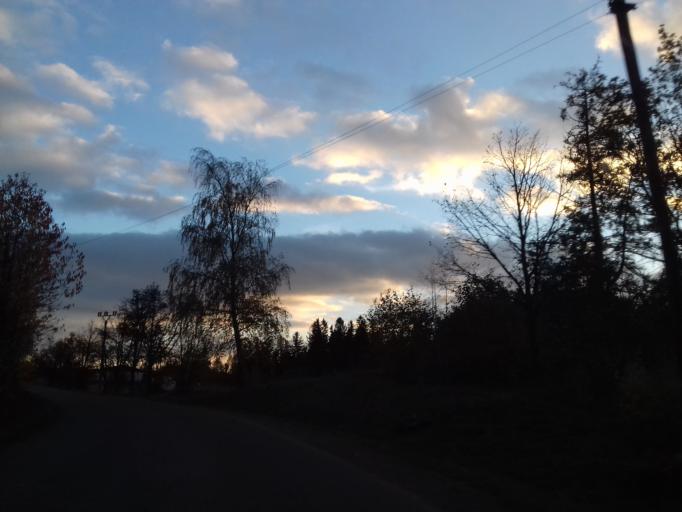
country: CZ
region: Pardubicky
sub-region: Okres Chrudim
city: Skutec
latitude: 49.8108
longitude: 15.9568
